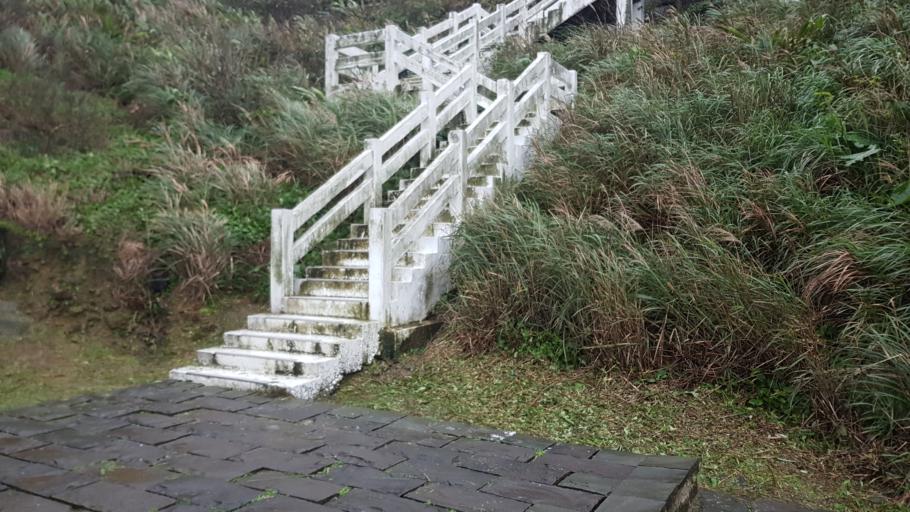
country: TW
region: Taiwan
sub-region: Keelung
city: Keelung
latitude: 25.1456
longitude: 121.7986
